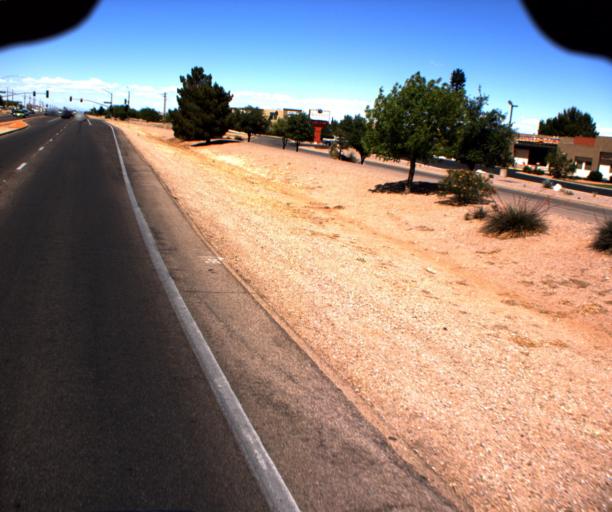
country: US
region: Arizona
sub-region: Cochise County
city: Sierra Vista
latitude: 31.5309
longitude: -110.2573
